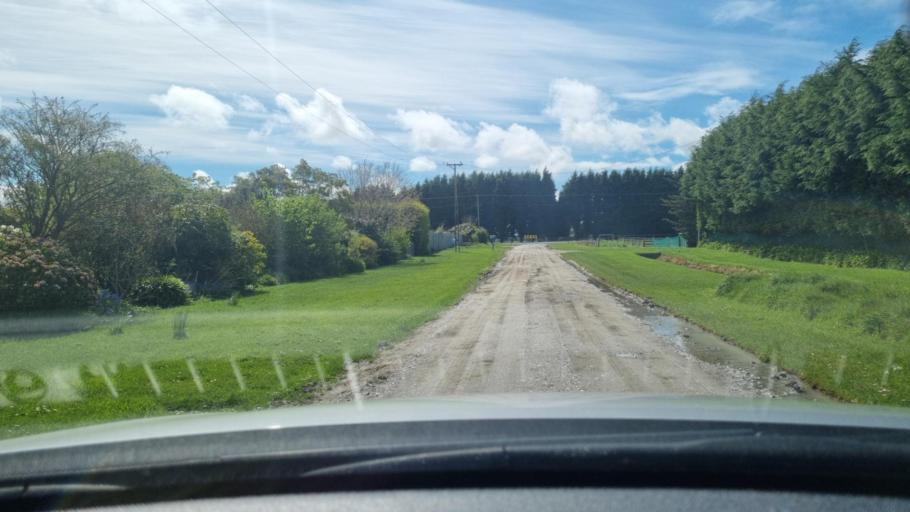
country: NZ
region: Southland
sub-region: Invercargill City
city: Invercargill
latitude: -46.4766
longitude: 168.3914
